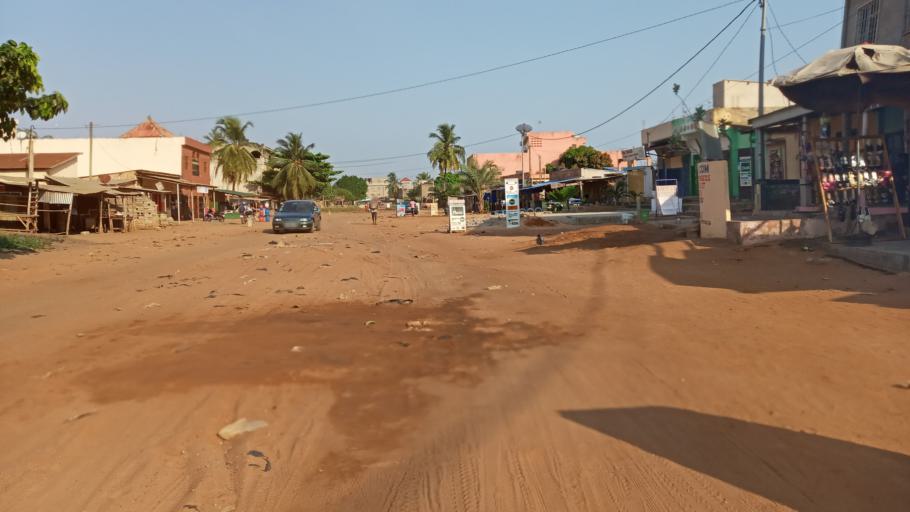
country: TG
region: Maritime
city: Lome
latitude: 6.1805
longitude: 1.1600
